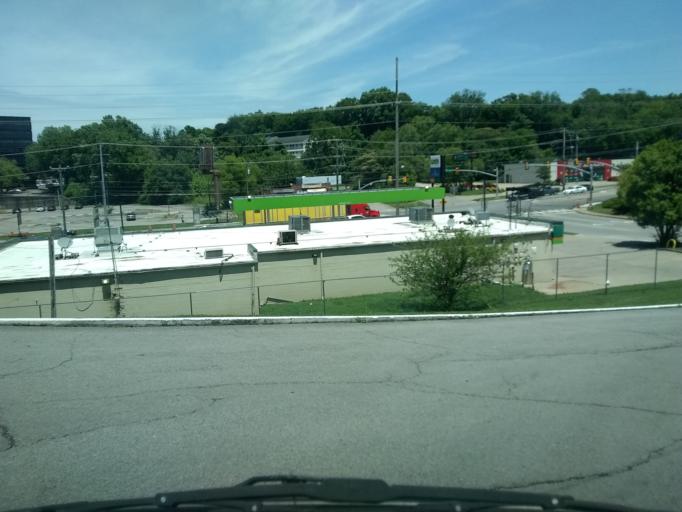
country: US
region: Tennessee
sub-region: Davidson County
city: Oak Hill
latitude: 36.1204
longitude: -86.7048
